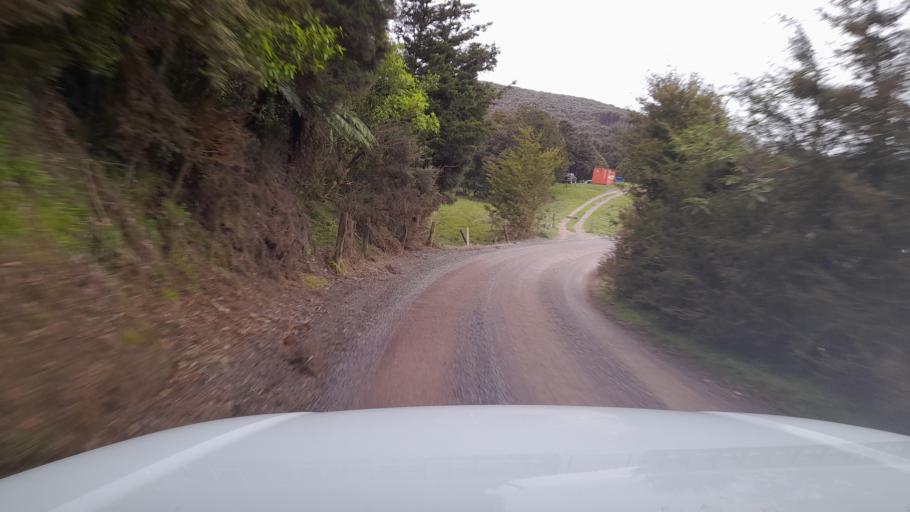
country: NZ
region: Northland
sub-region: Far North District
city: Paihia
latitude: -35.3488
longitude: 174.2254
